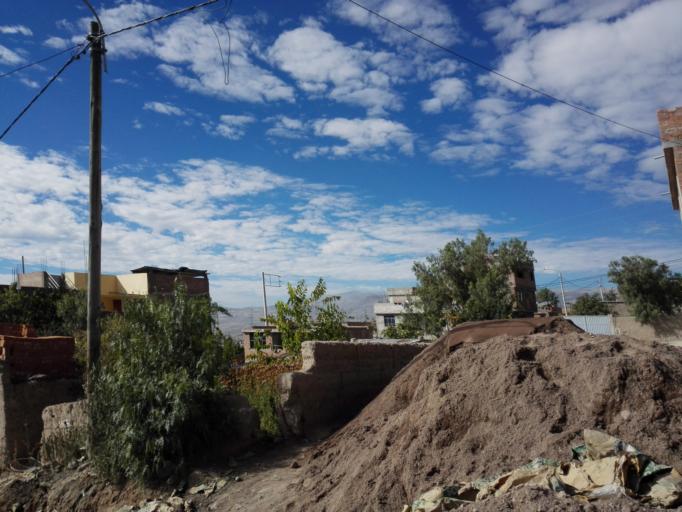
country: PE
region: Ayacucho
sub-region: Provincia de Huamanga
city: Ayacucho
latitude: -13.1385
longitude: -74.2334
